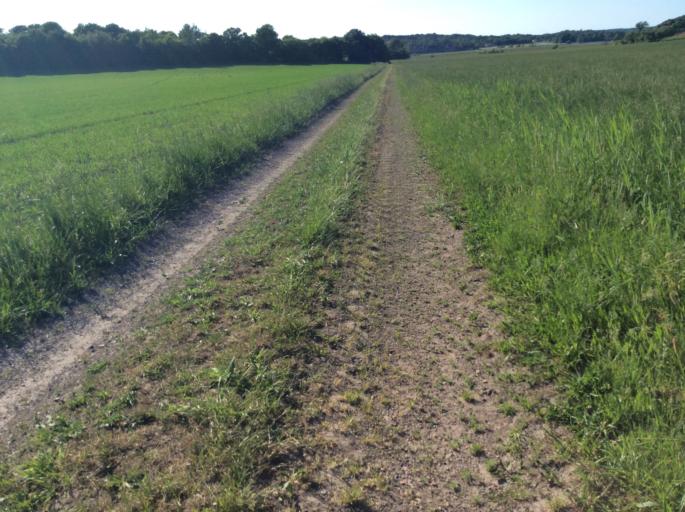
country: SE
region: Vaestra Goetaland
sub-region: Goteborg
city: Majorna
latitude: 57.7974
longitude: 11.8760
